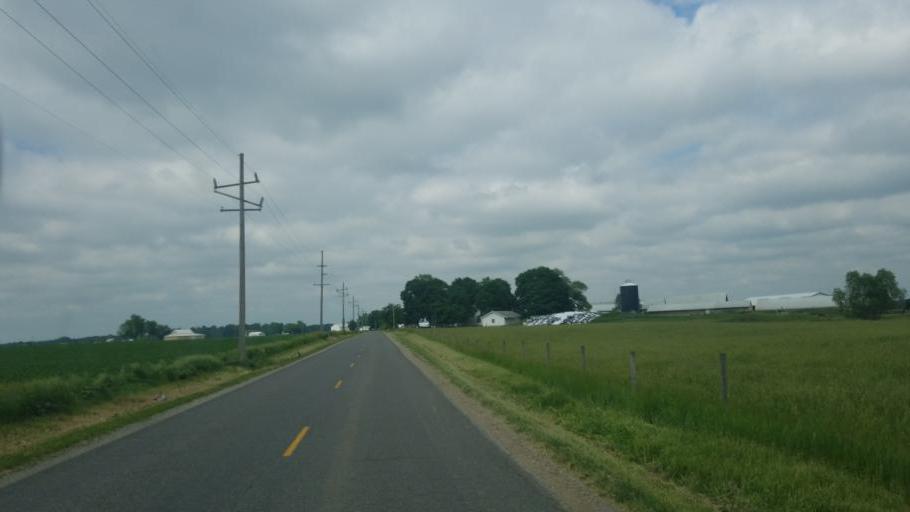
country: US
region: Indiana
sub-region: Elkhart County
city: Wakarusa
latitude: 41.4886
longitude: -86.0315
